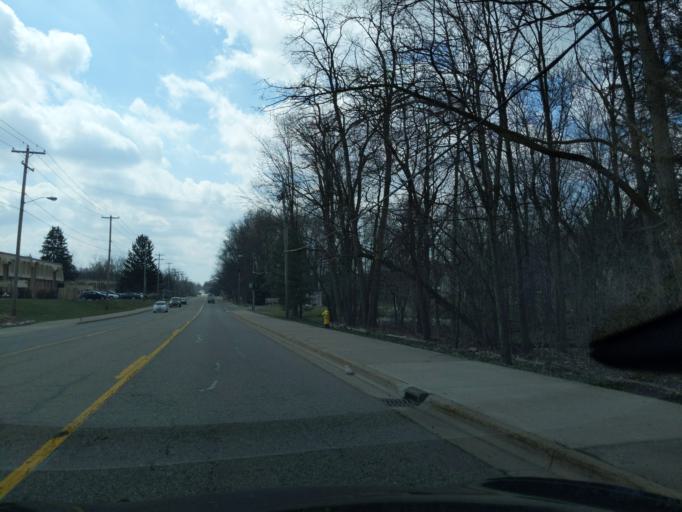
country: US
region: Michigan
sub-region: Calhoun County
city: Lakeview
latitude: 42.2558
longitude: -85.1987
